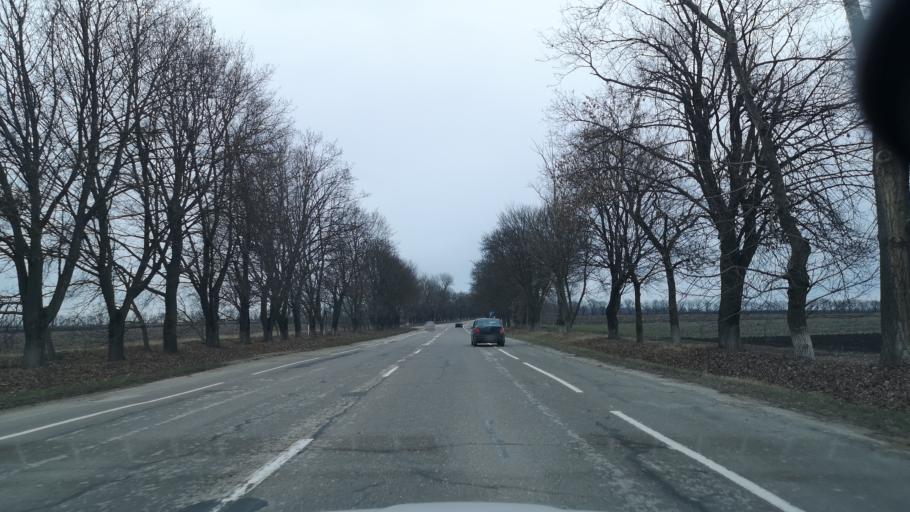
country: MD
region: Raionul Edinet
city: Edinet
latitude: 48.2373
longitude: 27.2067
